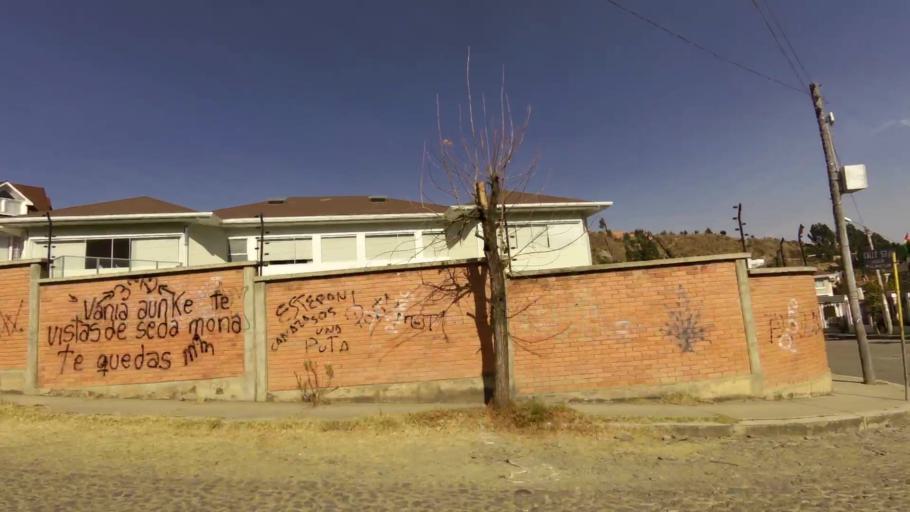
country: BO
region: La Paz
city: La Paz
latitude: -16.5091
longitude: -68.0546
